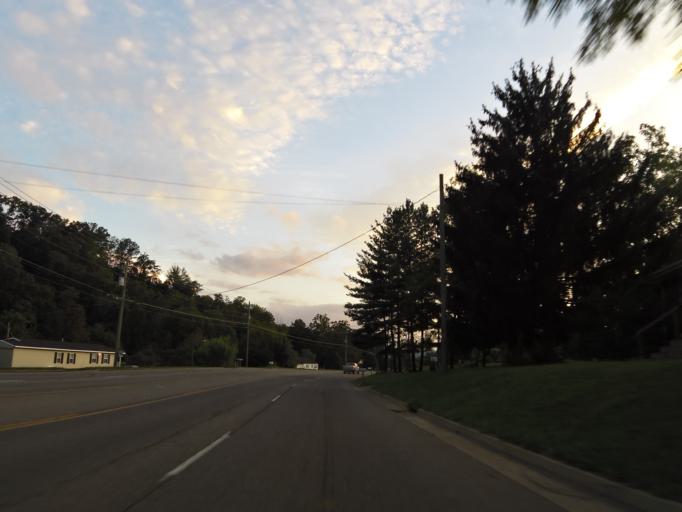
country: US
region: Tennessee
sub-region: Carter County
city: Hunter
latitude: 36.3781
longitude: -82.1518
